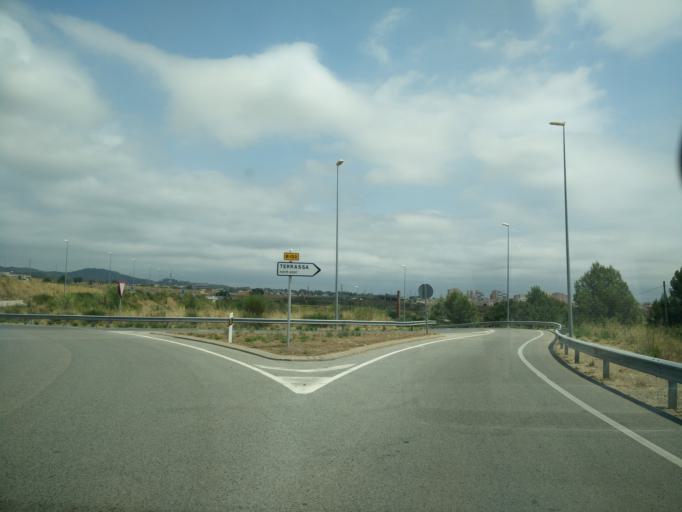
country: ES
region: Catalonia
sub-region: Provincia de Barcelona
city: Terrassa
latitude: 41.5830
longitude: 1.9928
